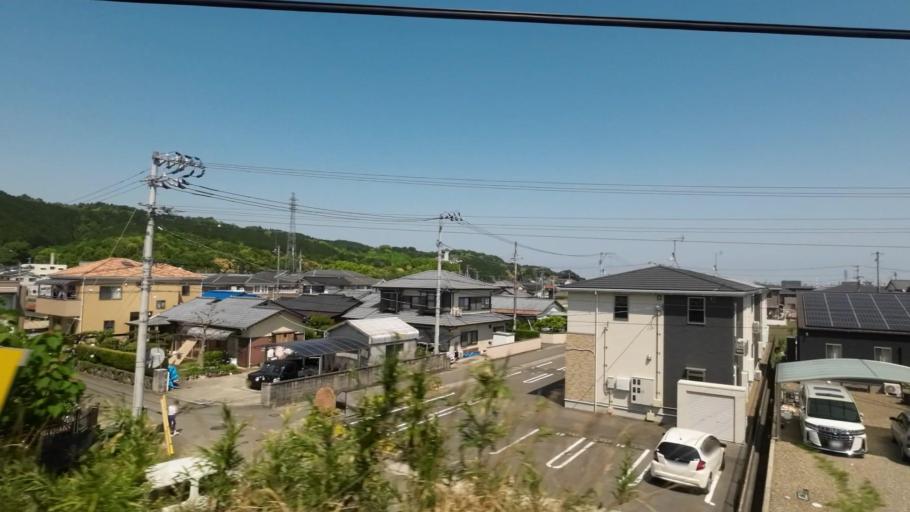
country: JP
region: Ehime
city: Niihama
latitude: 33.9407
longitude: 133.2865
